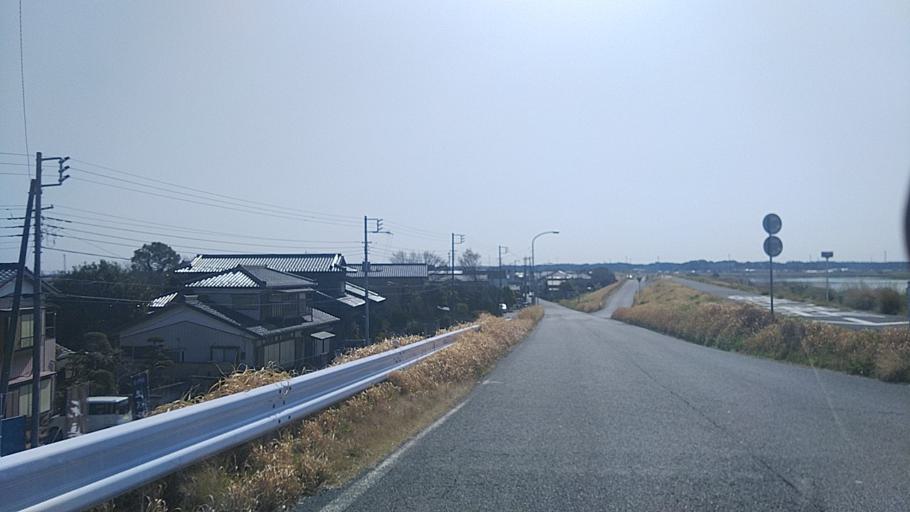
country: JP
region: Ibaraki
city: Ryugasaki
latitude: 35.8552
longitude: 140.1404
